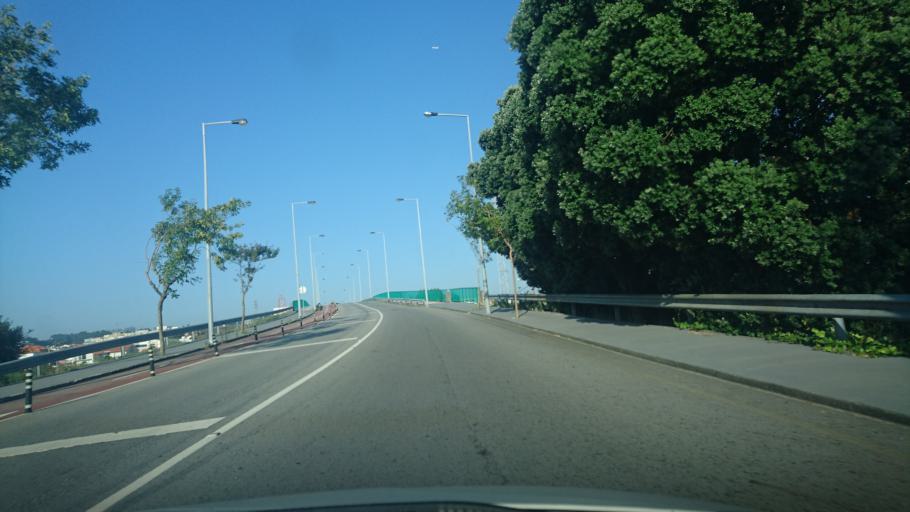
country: PT
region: Aveiro
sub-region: Ovar
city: Esmoriz
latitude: 40.9572
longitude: -8.6371
